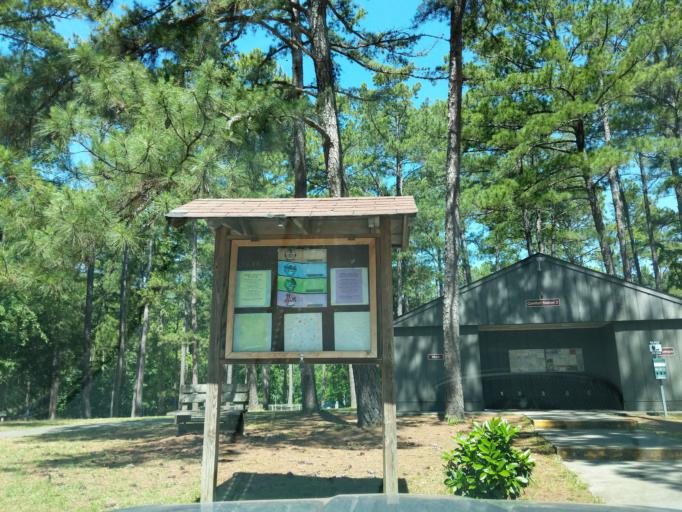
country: US
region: Georgia
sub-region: Columbia County
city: Appling
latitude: 33.6654
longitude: -82.3821
